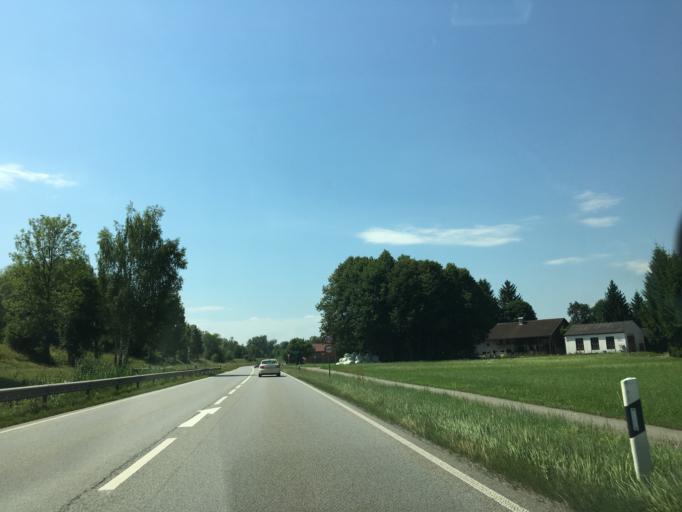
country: DE
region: Bavaria
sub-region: Upper Bavaria
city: Griesstatt
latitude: 48.0131
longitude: 12.1722
